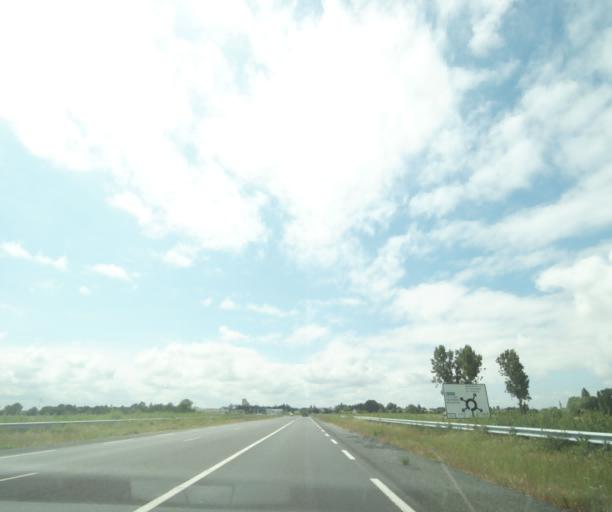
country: FR
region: Poitou-Charentes
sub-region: Departement des Deux-Sevres
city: Sainte-Verge
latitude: 47.0166
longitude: -0.2015
